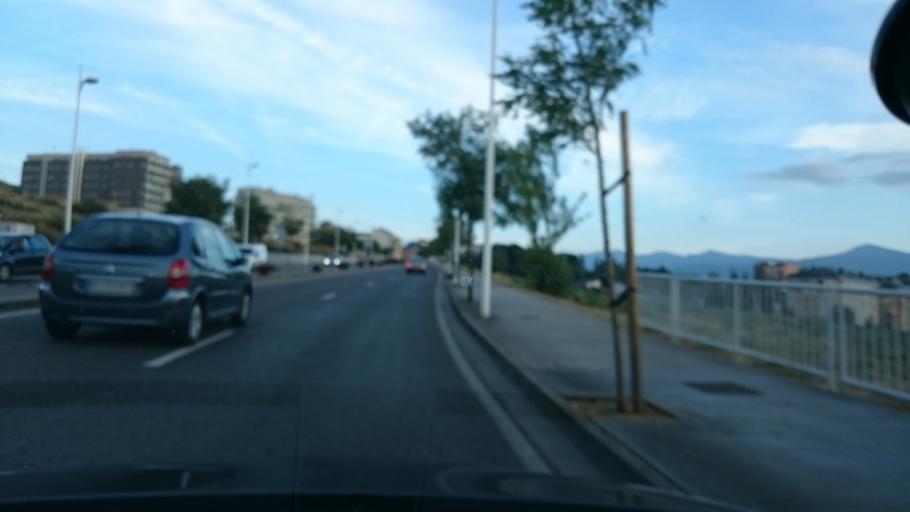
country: ES
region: Castille and Leon
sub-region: Provincia de Leon
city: Ponferrada
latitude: 42.5552
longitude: -6.5871
